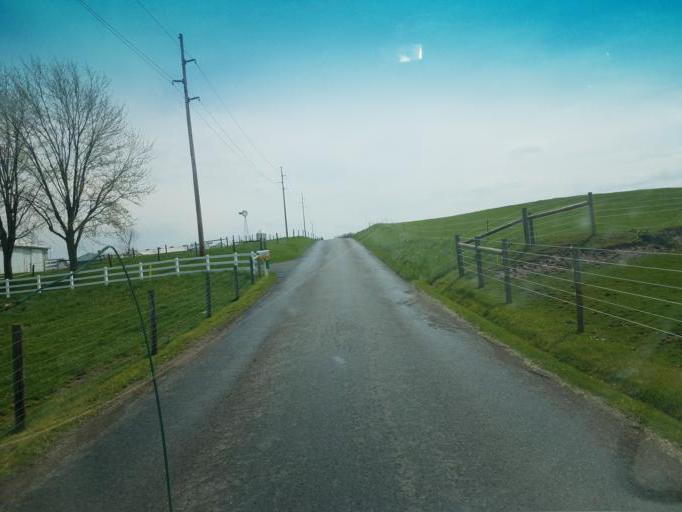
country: US
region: Ohio
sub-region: Holmes County
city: Millersburg
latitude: 40.5502
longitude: -81.8500
